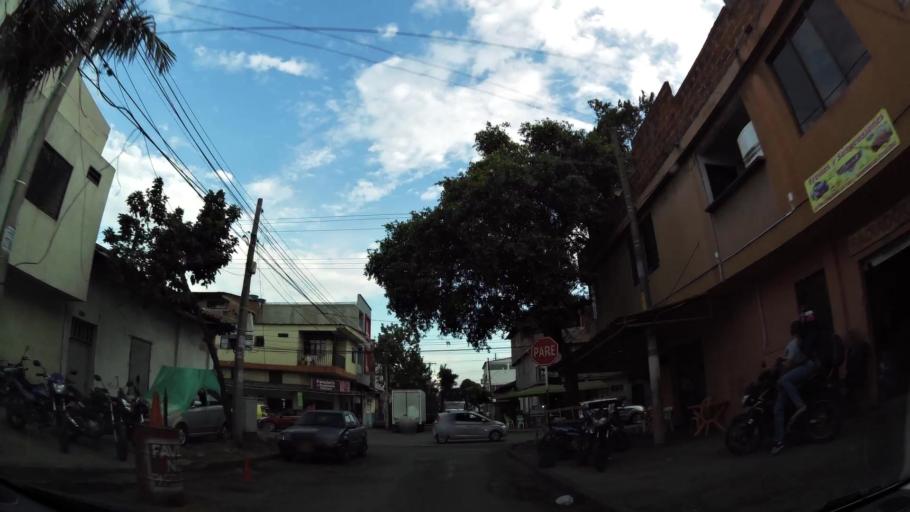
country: CO
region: Valle del Cauca
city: Cali
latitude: 3.4605
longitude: -76.5153
